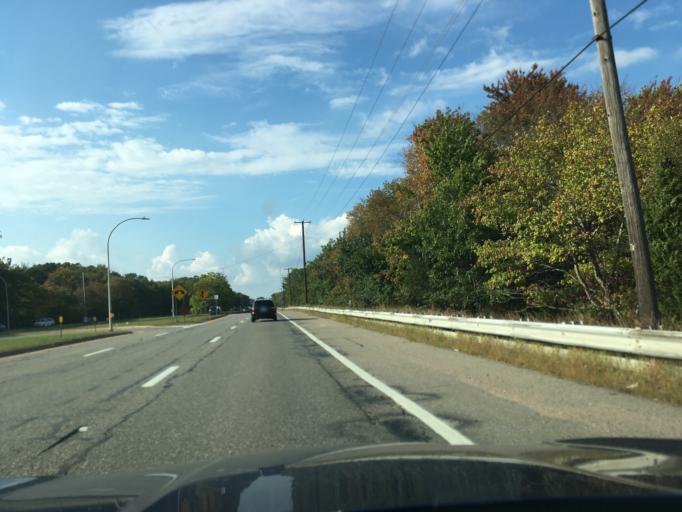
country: US
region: Rhode Island
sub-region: Bristol County
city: Barrington
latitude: 41.7669
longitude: -71.3219
